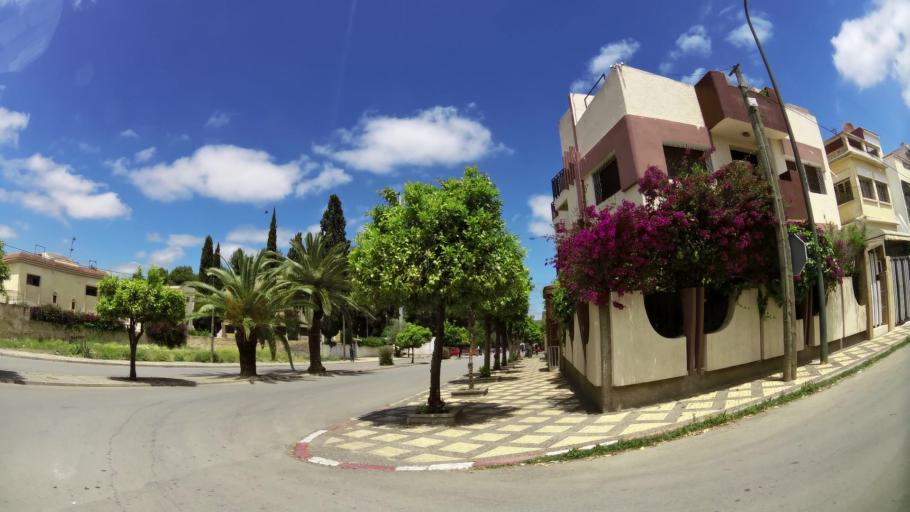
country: MA
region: Fes-Boulemane
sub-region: Fes
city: Fes
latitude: 34.0366
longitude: -5.0225
